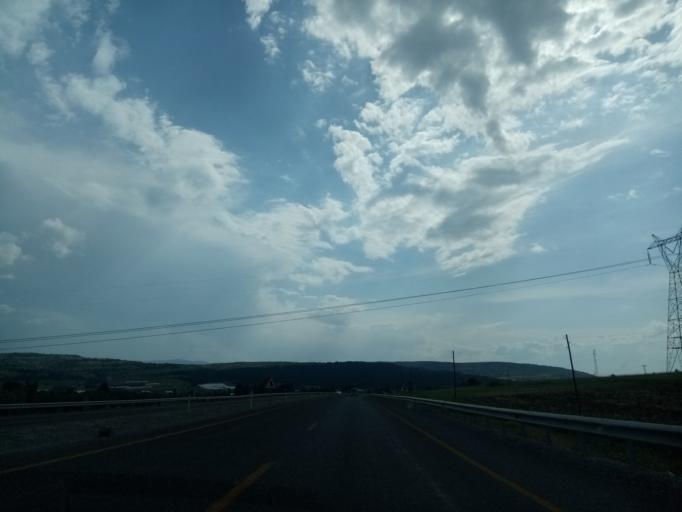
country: TR
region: Isparta
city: Bagkonak
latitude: 38.1975
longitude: 31.2498
